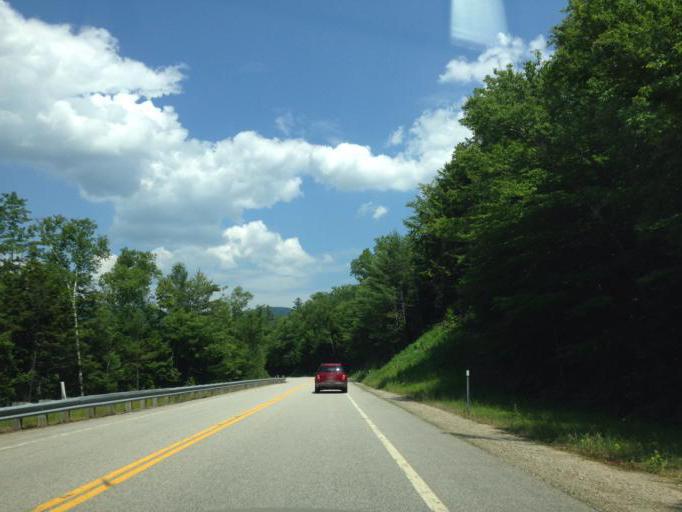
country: US
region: New Hampshire
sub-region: Carroll County
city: Tamworth
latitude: 44.0077
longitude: -71.2737
